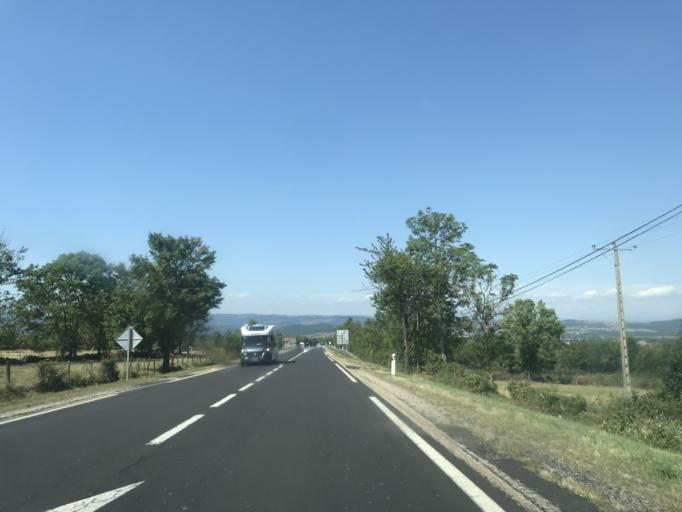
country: FR
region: Auvergne
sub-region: Departement de la Haute-Loire
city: Langeac
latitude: 45.1423
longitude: 3.5681
